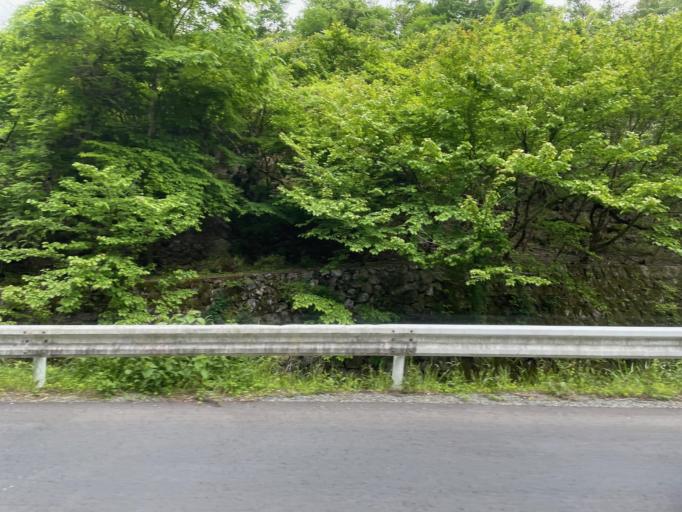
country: JP
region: Tochigi
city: Tanuma
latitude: 36.4635
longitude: 139.6012
